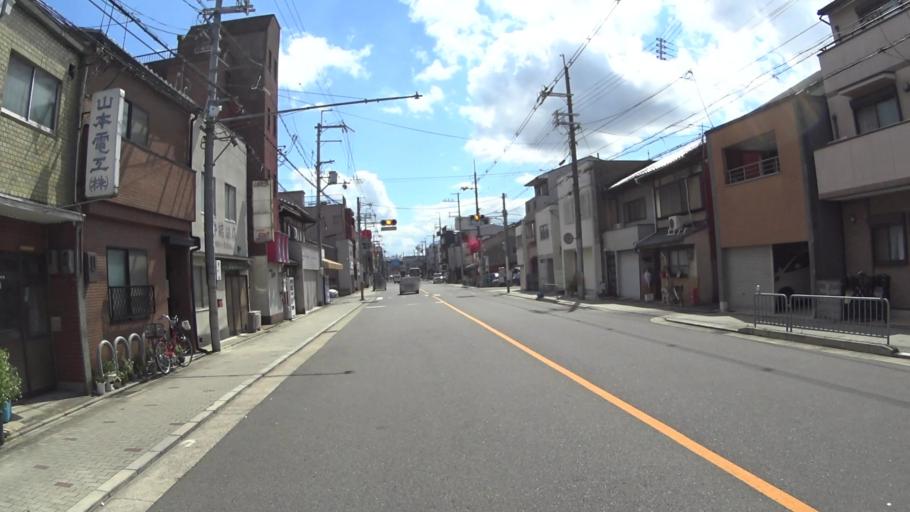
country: JP
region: Kyoto
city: Kyoto
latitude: 34.9755
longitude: 135.7618
